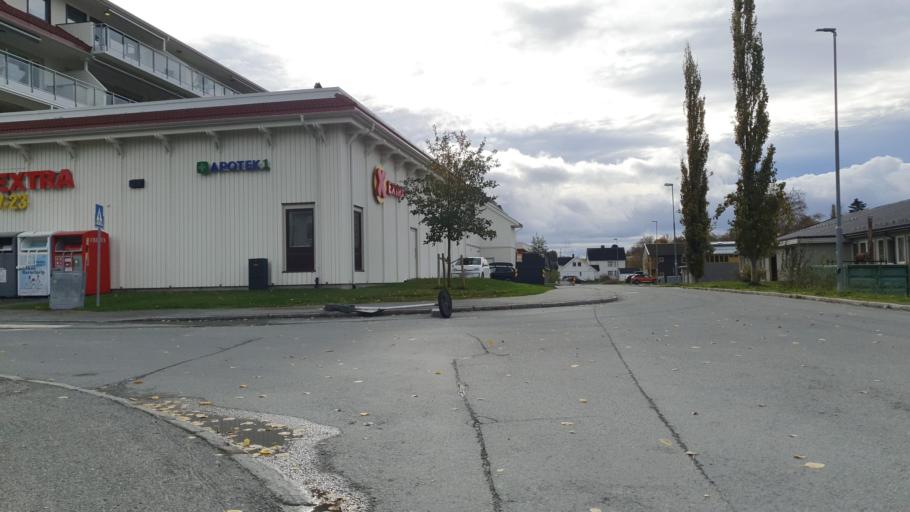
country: NO
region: Sor-Trondelag
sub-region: Klaebu
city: Klaebu
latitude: 63.2999
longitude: 10.4827
